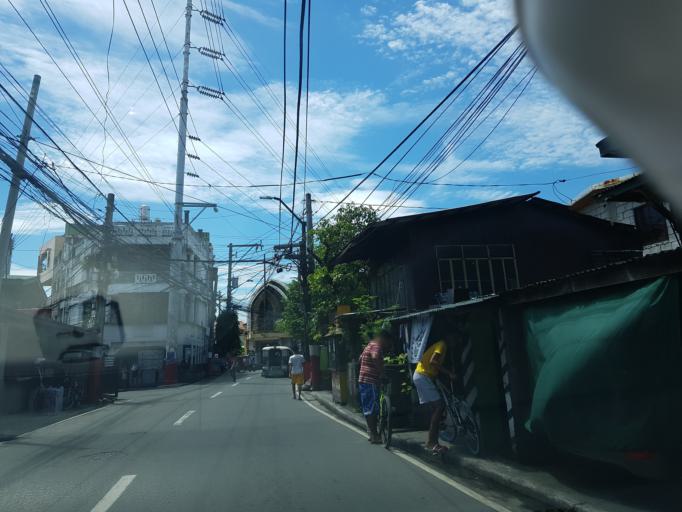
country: PH
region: Calabarzon
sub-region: Province of Rizal
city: Taguig
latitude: 14.5240
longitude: 121.0735
